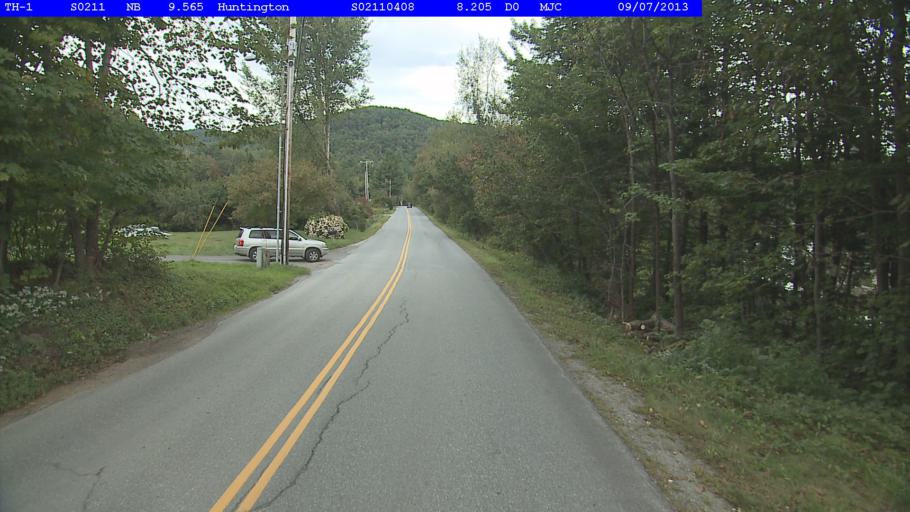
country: US
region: Vermont
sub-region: Chittenden County
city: Hinesburg
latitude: 44.3342
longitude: -72.9946
